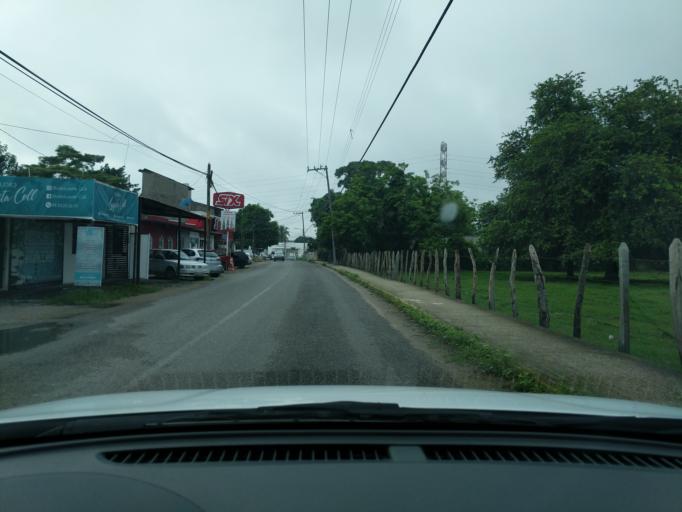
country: MX
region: Tabasco
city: Villahermosa
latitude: 17.9512
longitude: -92.9649
